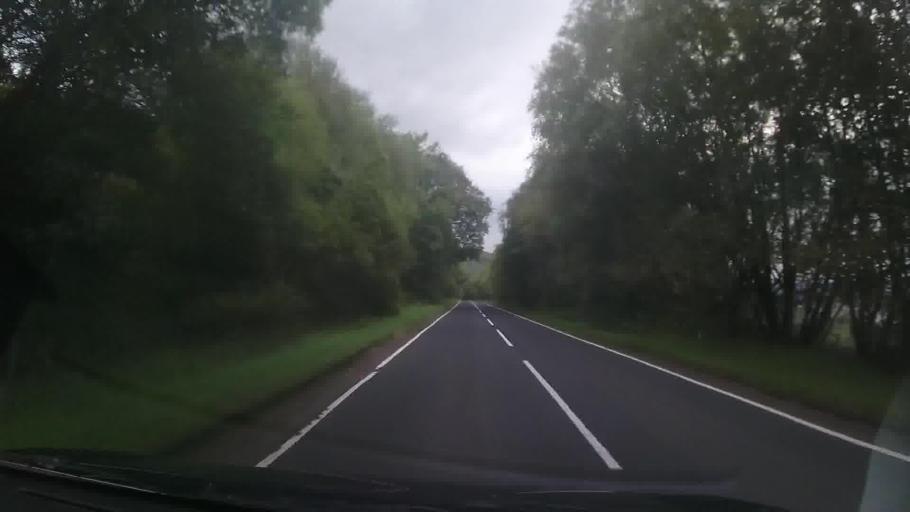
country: GB
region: Scotland
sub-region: Argyll and Bute
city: Garelochhead
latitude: 56.2289
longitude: -4.9783
